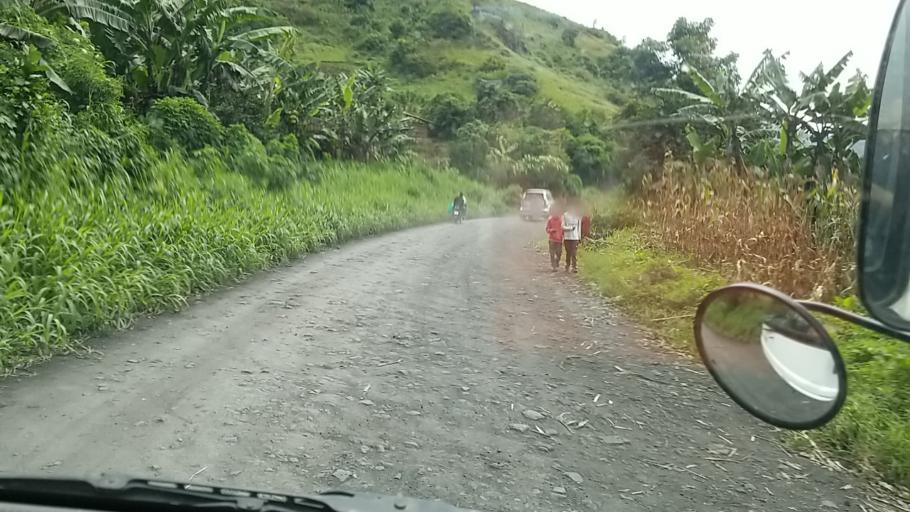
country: CD
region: Nord Kivu
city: Sake
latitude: -1.7371
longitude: 29.0070
